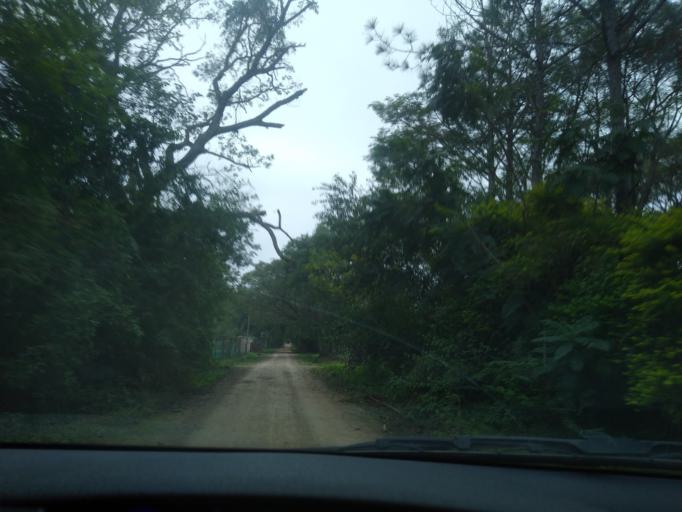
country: AR
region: Chaco
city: Colonia Benitez
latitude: -27.3319
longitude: -58.9543
